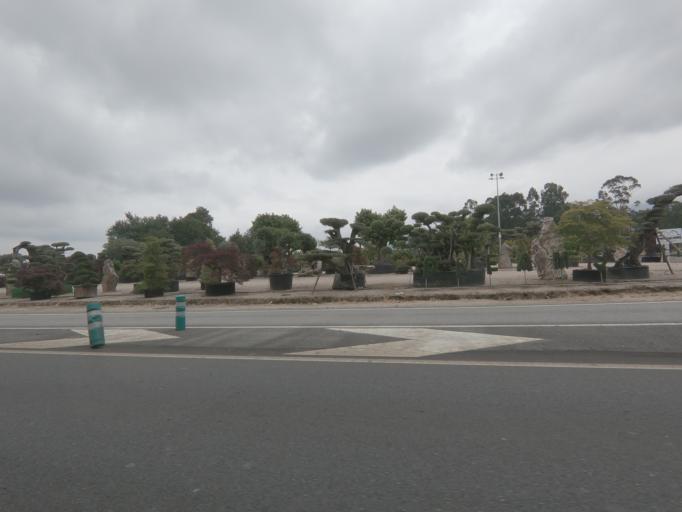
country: PT
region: Viana do Castelo
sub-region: Vila Nova de Cerveira
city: Vila Nova de Cerveira
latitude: 41.9585
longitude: -8.7641
